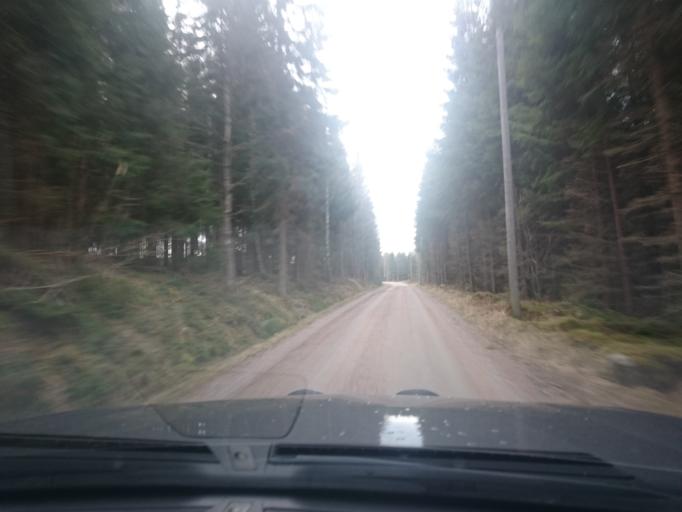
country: SE
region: Joenkoeping
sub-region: Vetlanda Kommun
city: Vetlanda
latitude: 57.2952
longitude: 15.1404
